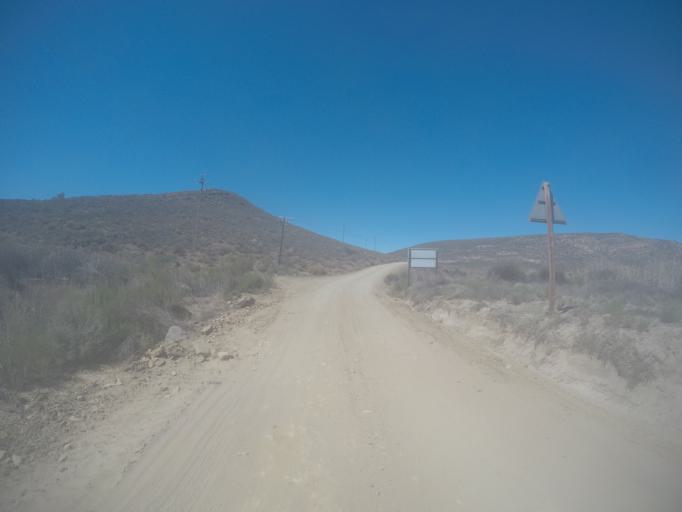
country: ZA
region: Western Cape
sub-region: West Coast District Municipality
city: Clanwilliam
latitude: -32.5199
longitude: 19.3509
